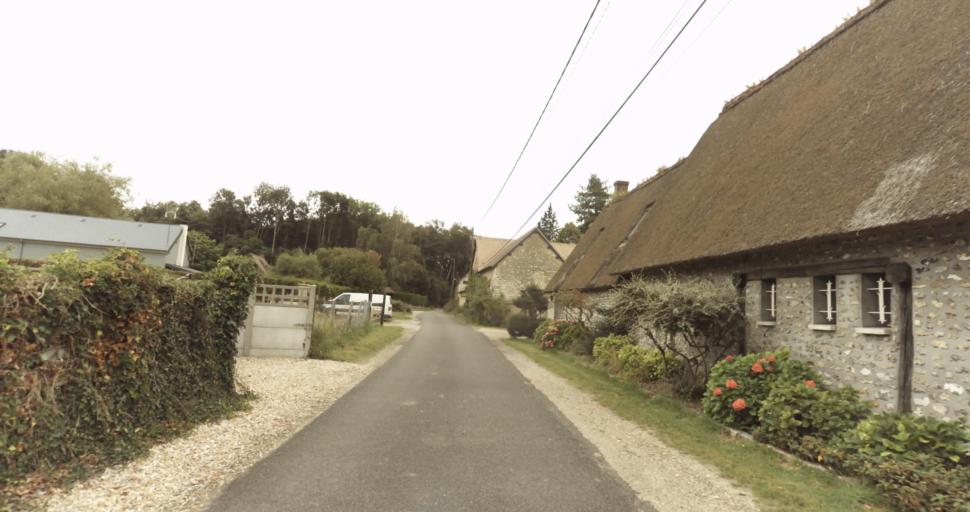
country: FR
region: Haute-Normandie
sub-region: Departement de l'Eure
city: Houlbec-Cocherel
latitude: 49.0780
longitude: 1.2849
